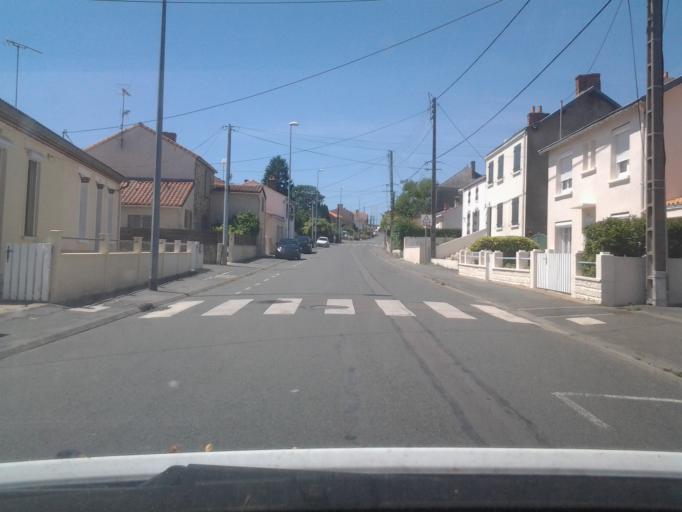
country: FR
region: Pays de la Loire
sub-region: Departement de la Vendee
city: La Roche-sur-Yon
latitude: 46.6619
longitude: -1.4035
